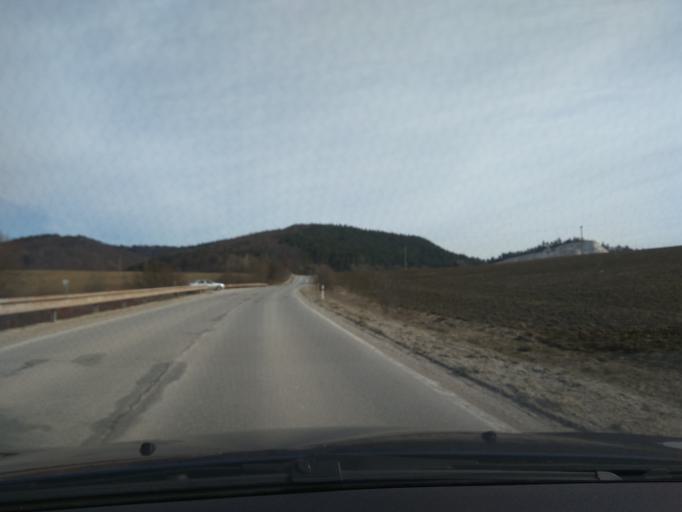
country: SK
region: Zilinsky
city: Rajec
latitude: 49.0910
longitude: 18.5948
